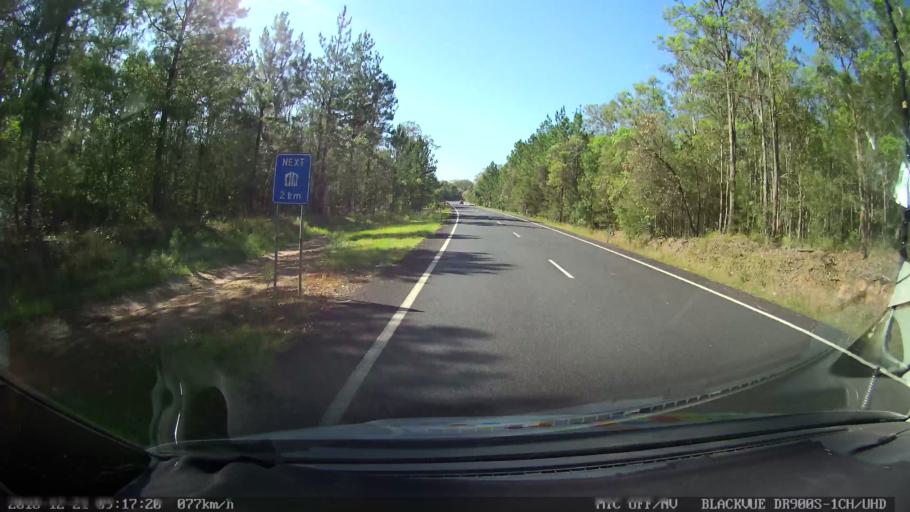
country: AU
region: New South Wales
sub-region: Clarence Valley
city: Maclean
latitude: -29.2912
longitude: 152.9901
